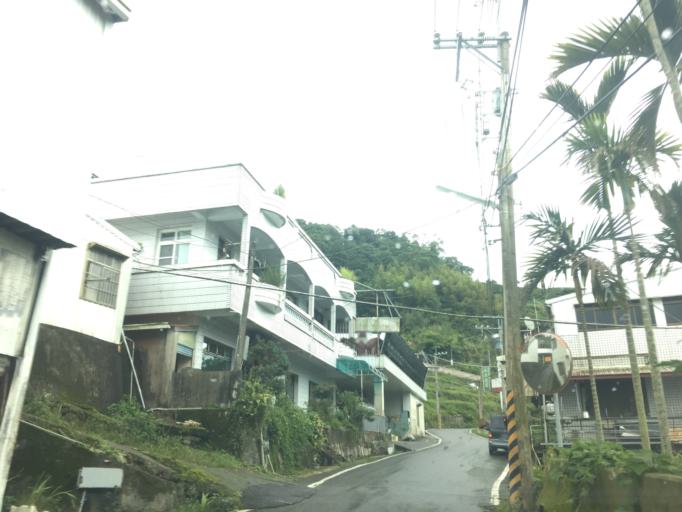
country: TW
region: Taiwan
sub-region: Yunlin
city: Douliu
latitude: 23.5615
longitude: 120.6606
